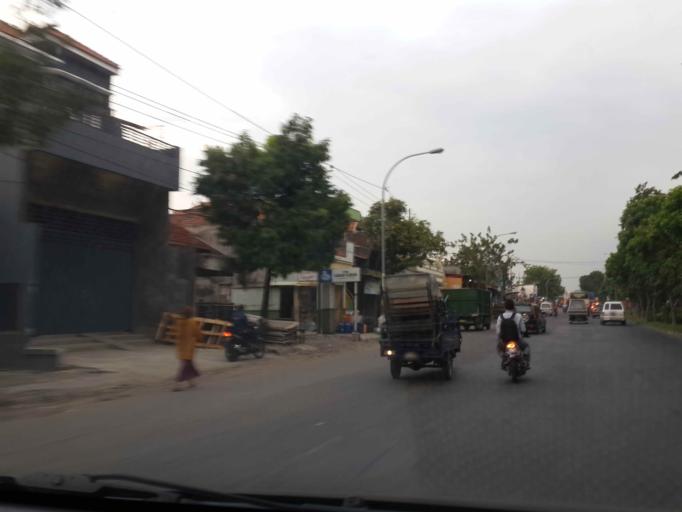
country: ID
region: East Java
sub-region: Kota Surabaya
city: Surabaya
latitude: -7.2450
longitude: 112.7164
